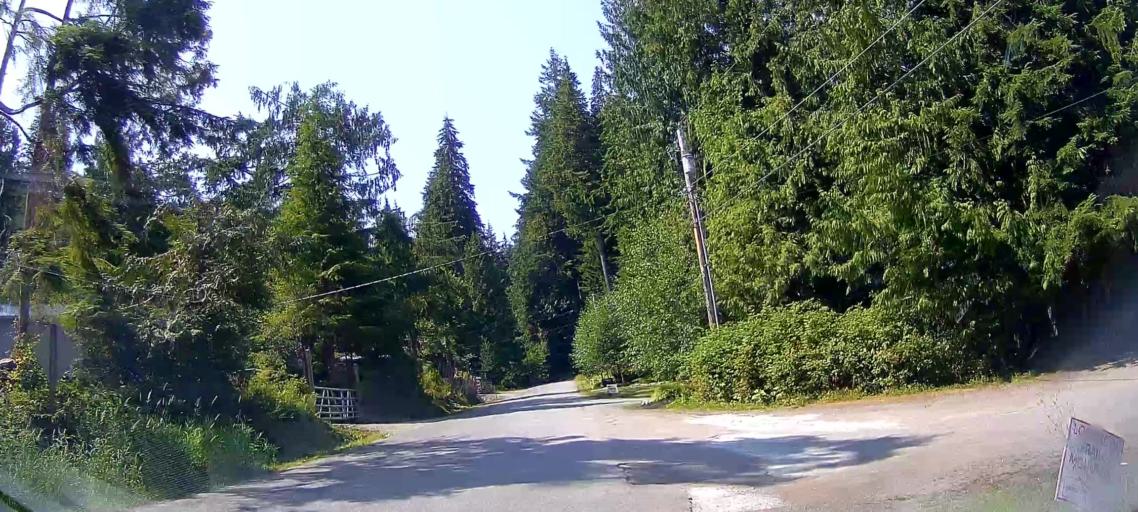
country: US
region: Washington
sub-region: Snohomish County
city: Arlington Heights
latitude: 48.3105
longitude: -121.9891
